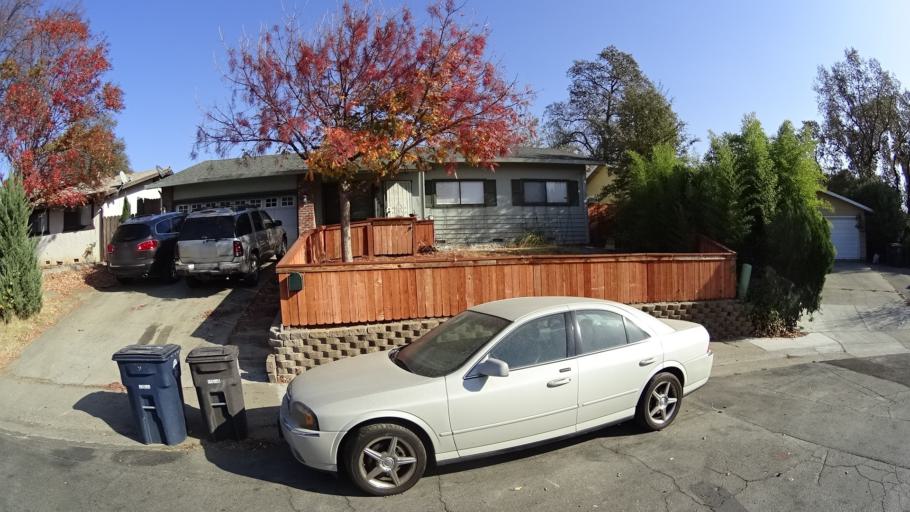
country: US
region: California
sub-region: Sacramento County
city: Citrus Heights
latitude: 38.6763
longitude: -121.2822
